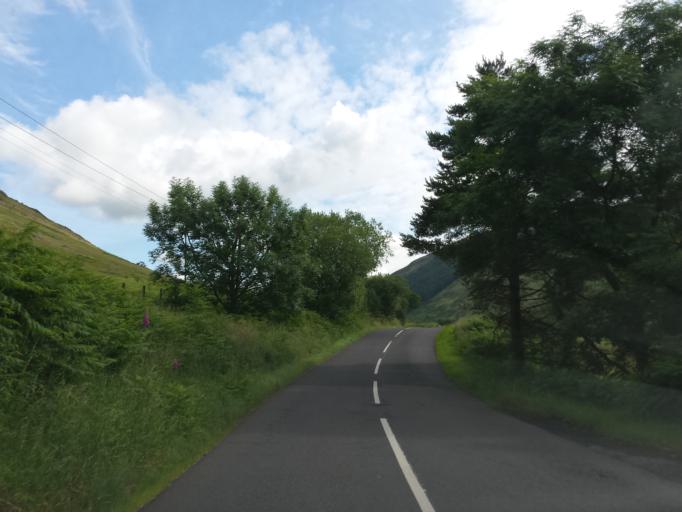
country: GB
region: Scotland
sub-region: Dumfries and Galloway
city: Moffat
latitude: 55.3793
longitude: -3.3402
